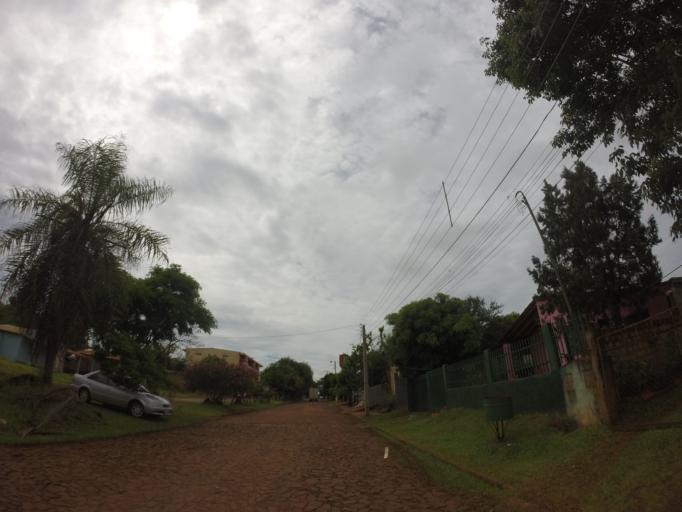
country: PY
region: Alto Parana
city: Ciudad del Este
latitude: -25.3838
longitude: -54.6578
